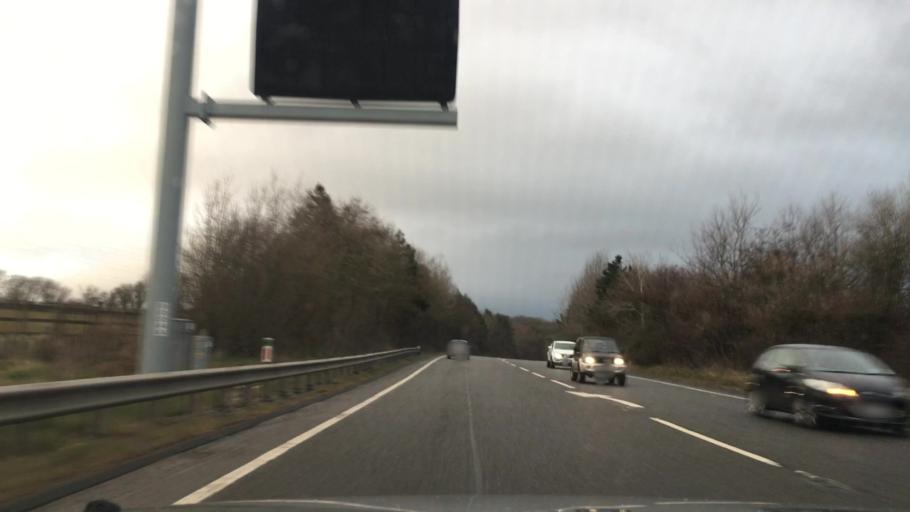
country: GB
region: England
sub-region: Cumbria
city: Askam in Furness
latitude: 54.1592
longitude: -3.2065
